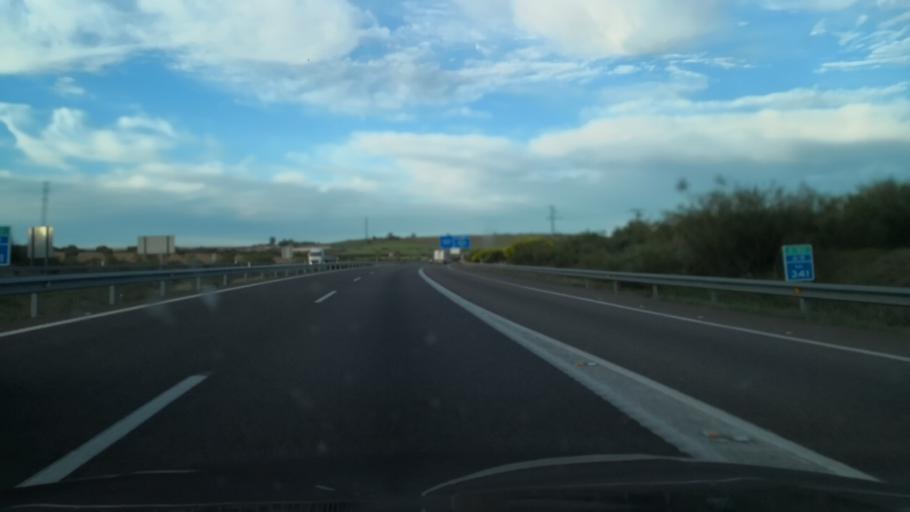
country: ES
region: Extremadura
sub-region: Provincia de Badajoz
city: Merida
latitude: 38.9394
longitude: -6.3617
